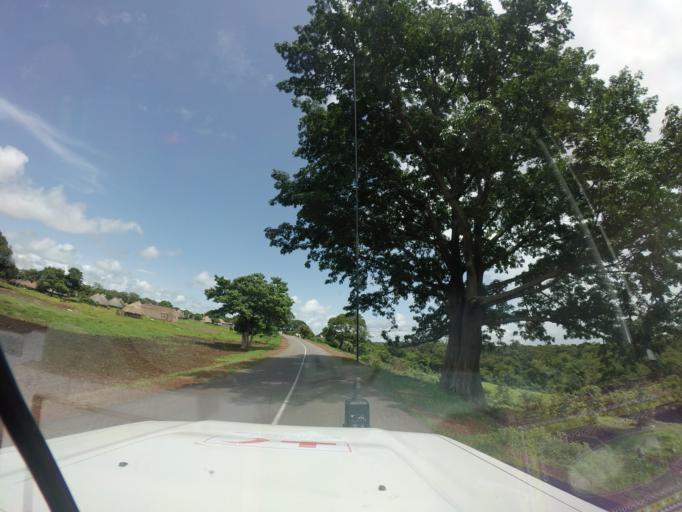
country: GN
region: Faranah
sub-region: Faranah Prefecture
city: Faranah
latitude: 10.0200
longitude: -10.8324
